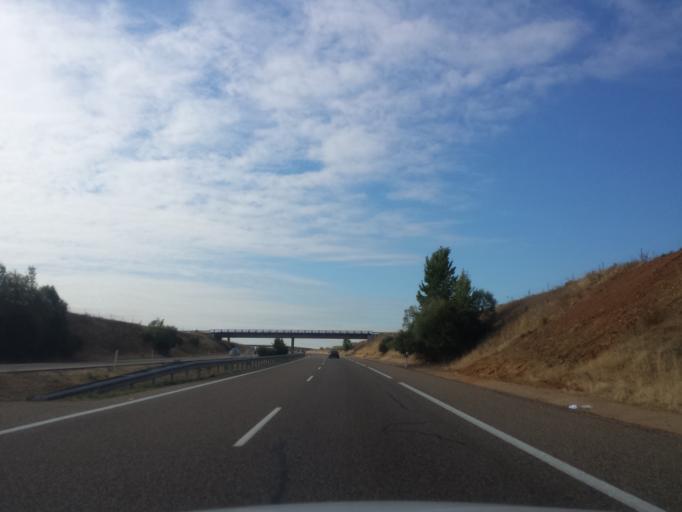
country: ES
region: Castille and Leon
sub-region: Provincia de Leon
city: Onzonilla
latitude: 42.4886
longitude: -5.5994
